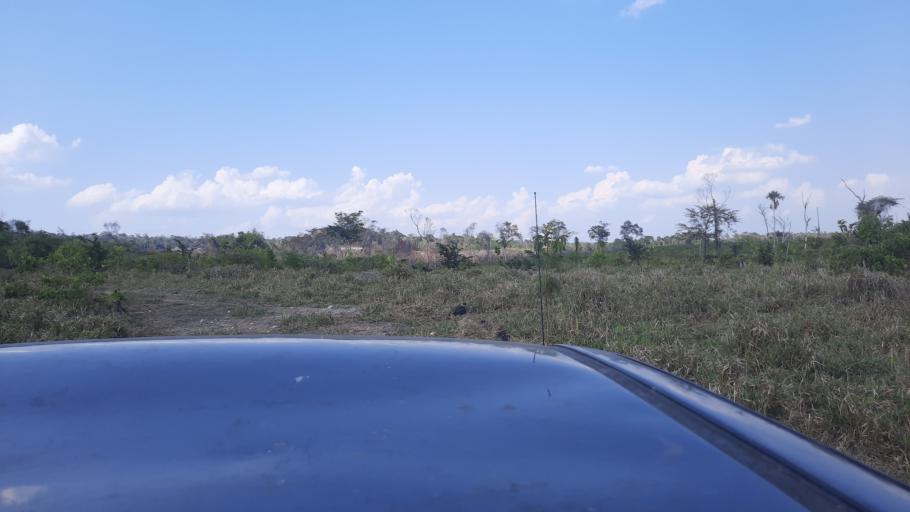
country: BZ
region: Cayo
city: Valley of Peace
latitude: 17.4029
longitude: -89.0393
